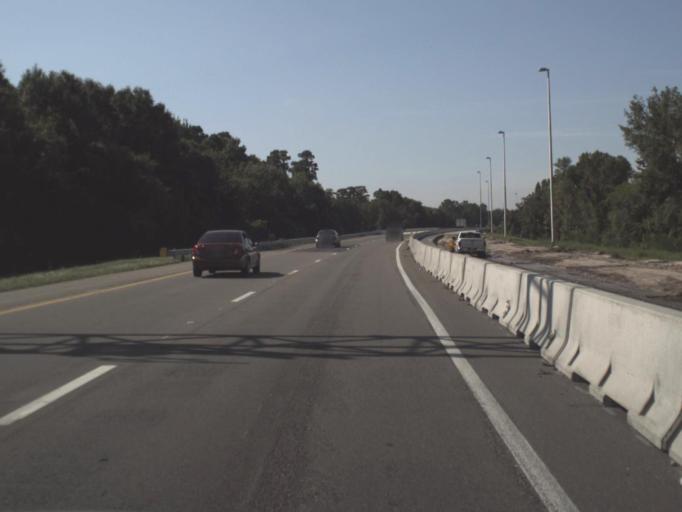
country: US
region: Florida
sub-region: Hillsborough County
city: Pebble Creek
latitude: 28.0898
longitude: -82.3553
